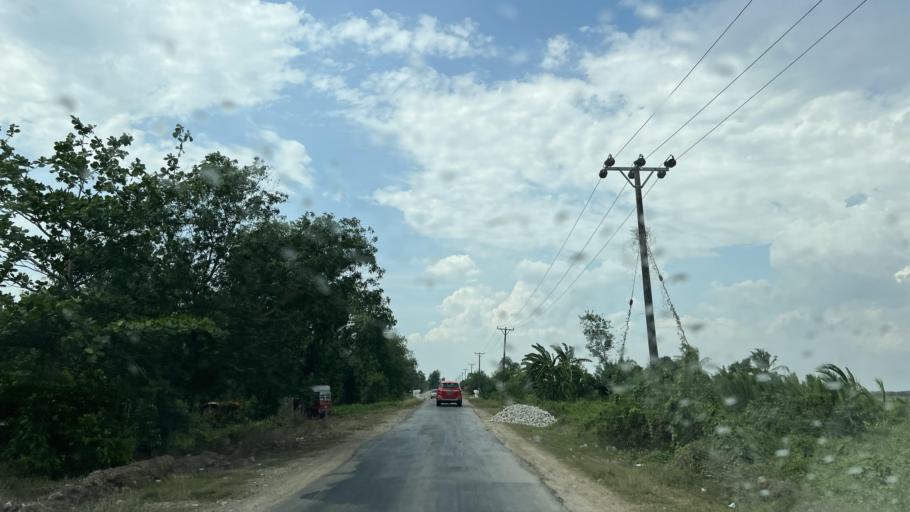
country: MM
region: Ayeyarwady
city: Pyapon
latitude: 16.2312
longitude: 95.6951
